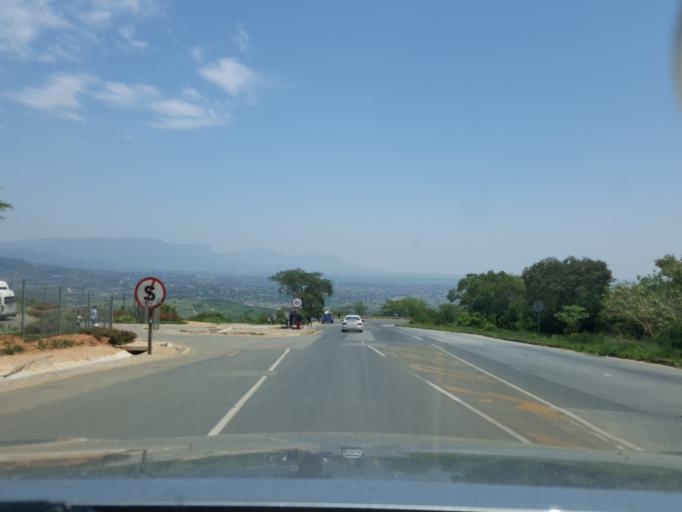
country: ZA
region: Limpopo
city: Thulamahashi
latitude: -24.8333
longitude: 31.0703
